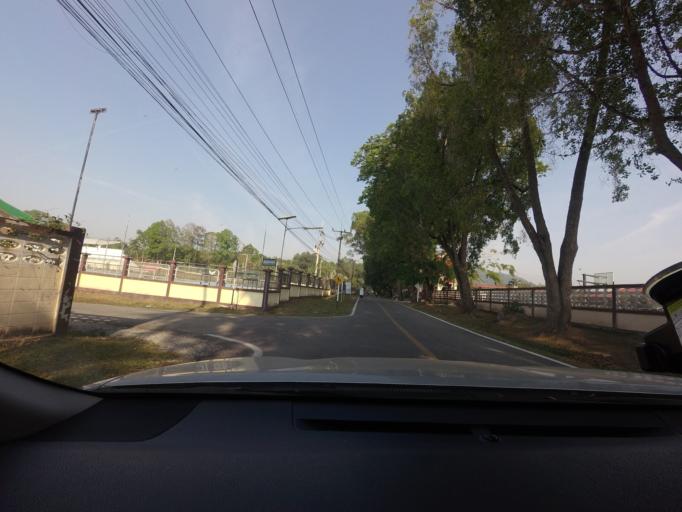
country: TH
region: Narathiwat
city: Rueso
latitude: 6.3989
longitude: 101.5252
